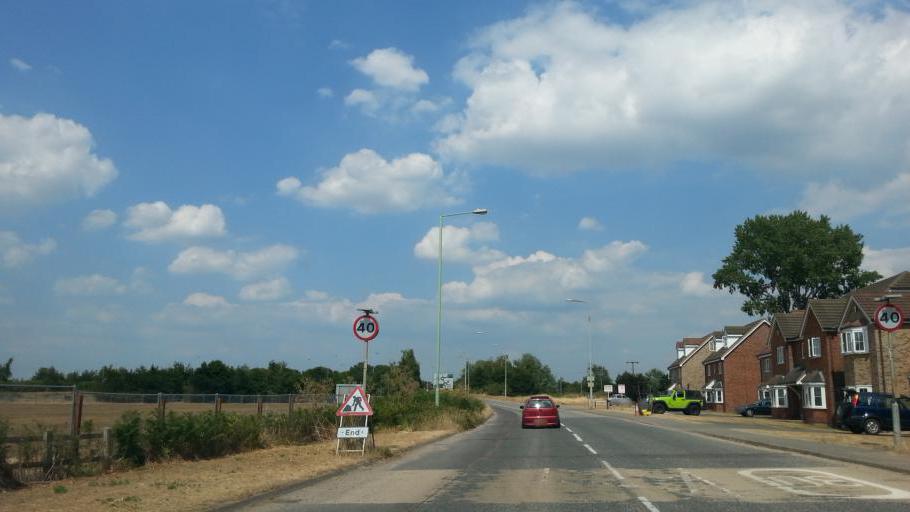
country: GB
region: England
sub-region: Cambridgeshire
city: Isleham
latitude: 52.3084
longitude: 0.4919
